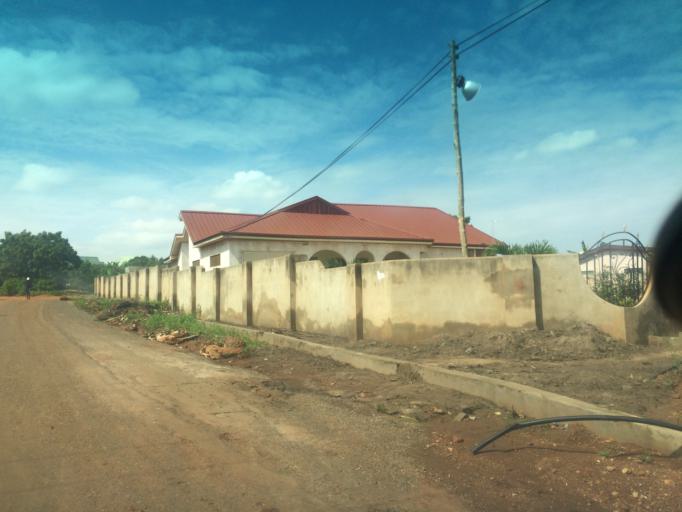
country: GH
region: Greater Accra
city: Medina Estates
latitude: 5.7415
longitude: -0.1728
